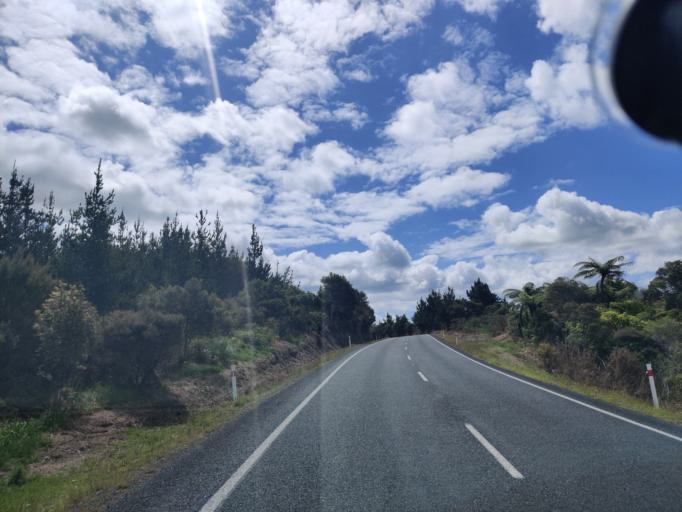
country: NZ
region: Northland
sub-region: Far North District
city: Kerikeri
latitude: -35.1366
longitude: 173.8790
